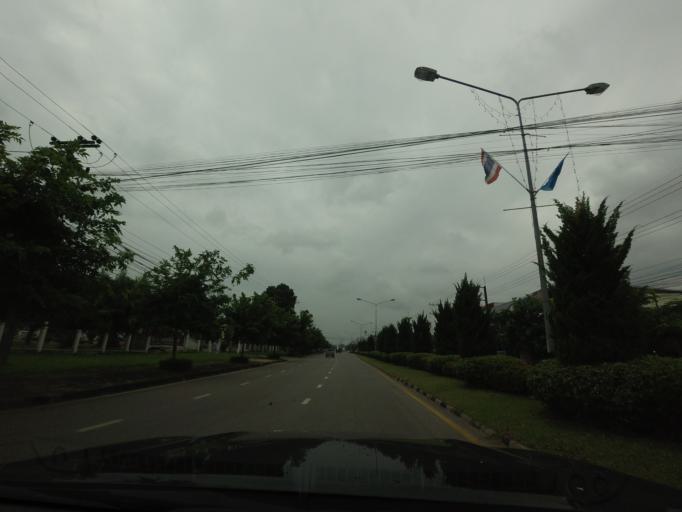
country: TH
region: Nong Khai
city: Si Chiang Mai
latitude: 17.9574
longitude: 102.5890
